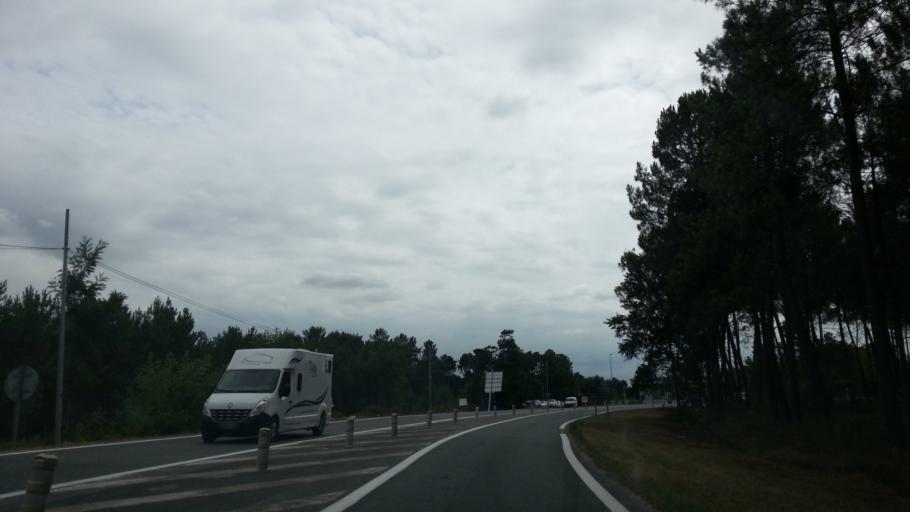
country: FR
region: Aquitaine
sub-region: Departement de la Gironde
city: Illats
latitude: 44.6094
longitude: -0.3662
